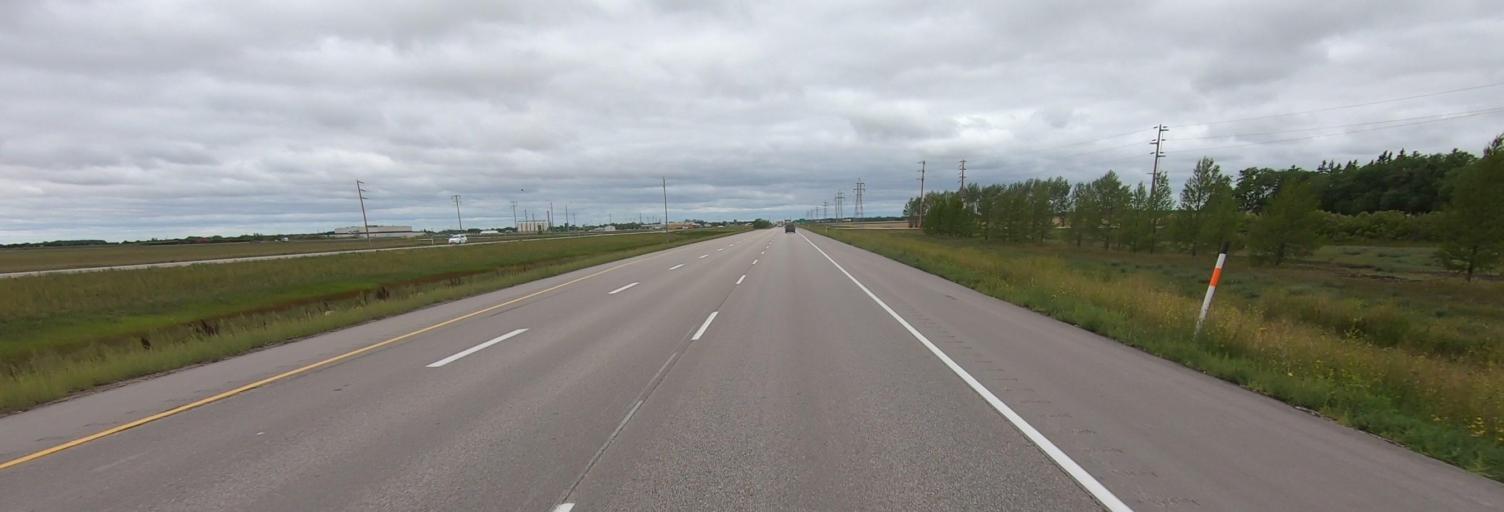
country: CA
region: Manitoba
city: Headingley
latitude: 49.9004
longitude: -97.7215
